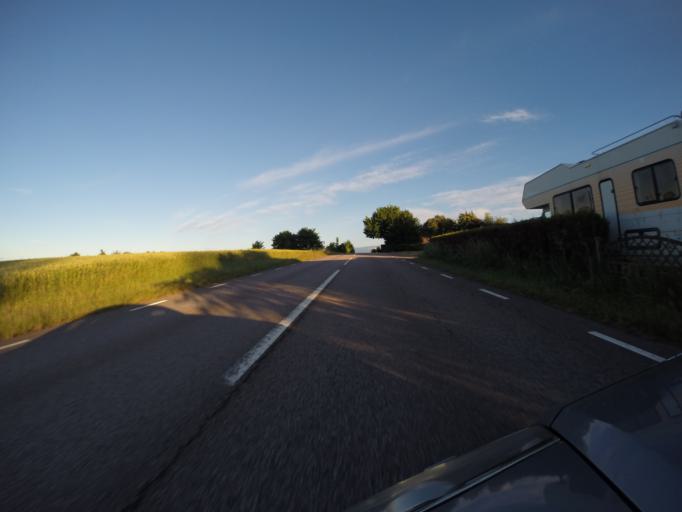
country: SE
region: Skane
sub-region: Angelholms Kommun
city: Strovelstorp
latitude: 56.1583
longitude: 12.8625
